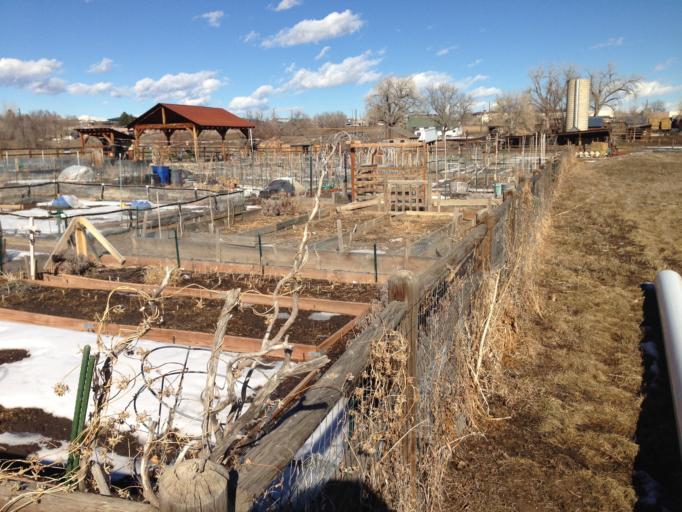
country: US
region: Colorado
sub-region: Boulder County
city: Louisville
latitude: 39.9836
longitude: -105.1257
